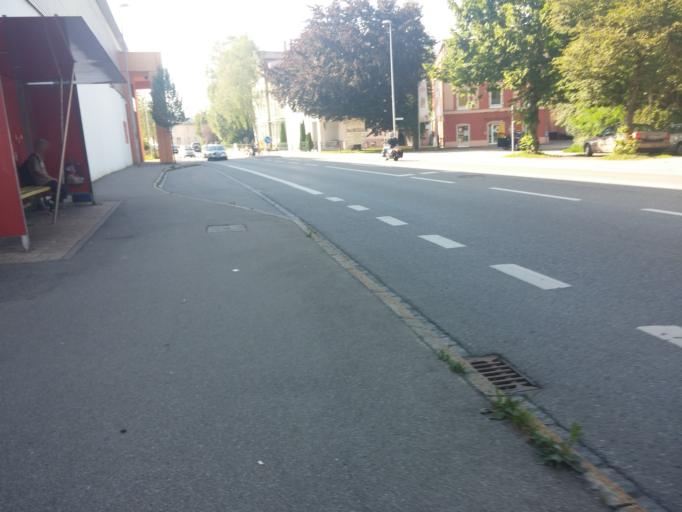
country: DE
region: Baden-Wuerttemberg
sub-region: Tuebingen Region
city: Leutkirch im Allgau
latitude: 47.8247
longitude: 10.0219
